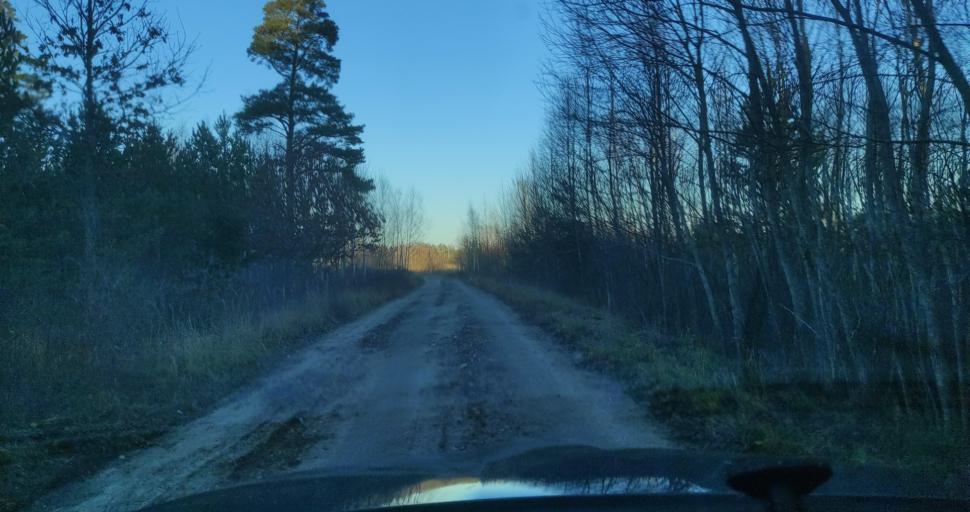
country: LV
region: Dundaga
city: Dundaga
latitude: 57.3836
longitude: 22.0832
